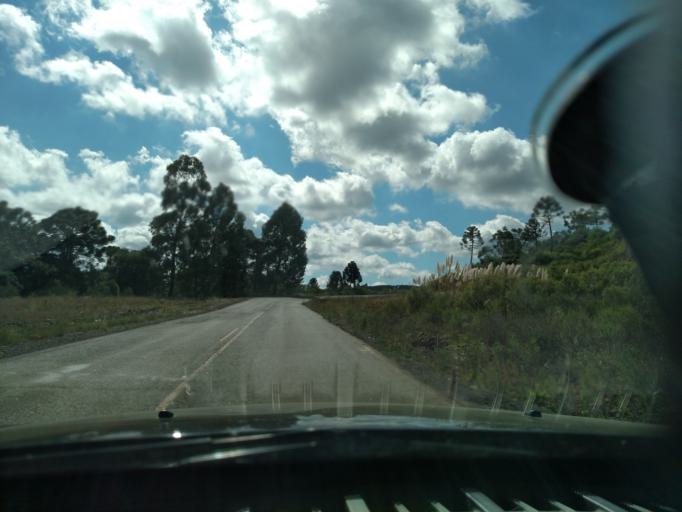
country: BR
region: Santa Catarina
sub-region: Sao Joaquim
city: Sao Joaquim
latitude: -28.0919
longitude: -50.0590
